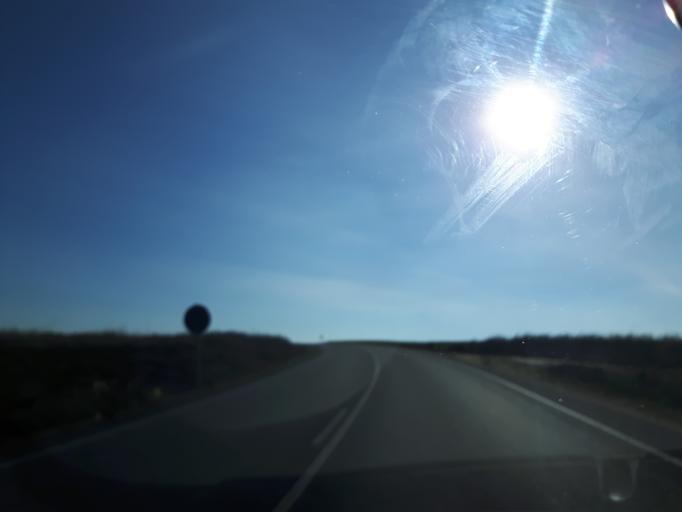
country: ES
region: Castille and Leon
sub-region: Provincia de Salamanca
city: San Cristobal de la Cuesta
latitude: 41.0242
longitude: -5.6237
